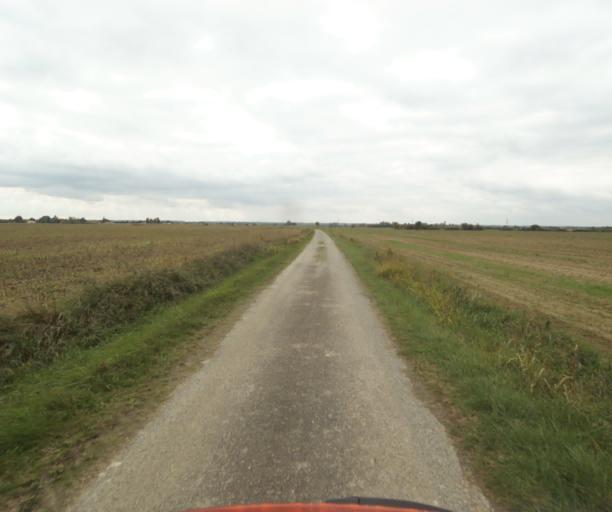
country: FR
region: Midi-Pyrenees
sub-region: Departement du Tarn-et-Garonne
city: Finhan
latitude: 43.8913
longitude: 1.2608
